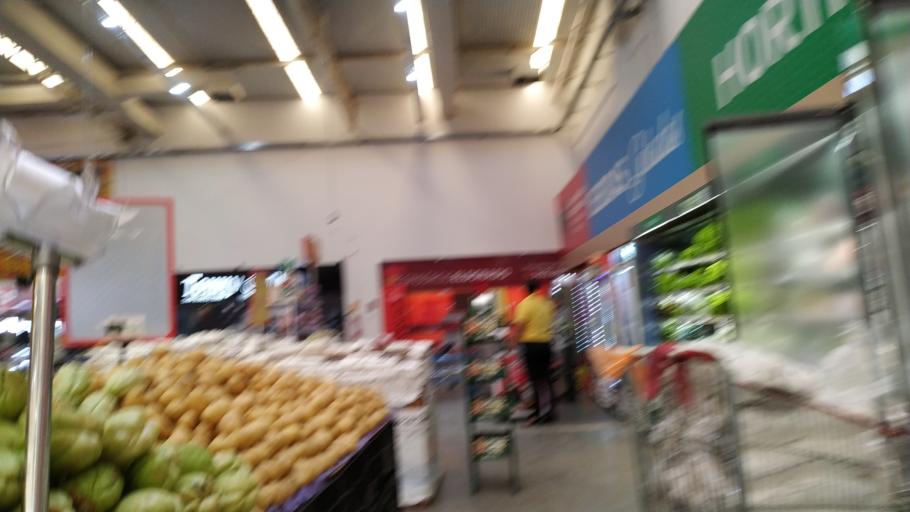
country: BR
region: Rio Grande do Norte
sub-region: Mossoro
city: Mossoro
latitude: -5.1904
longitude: -37.3355
